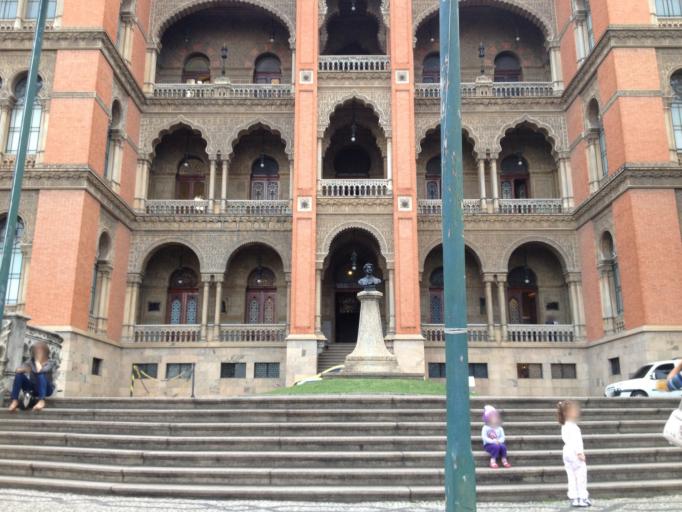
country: BR
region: Rio de Janeiro
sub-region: Rio De Janeiro
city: Rio de Janeiro
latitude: -22.8750
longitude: -43.2450
